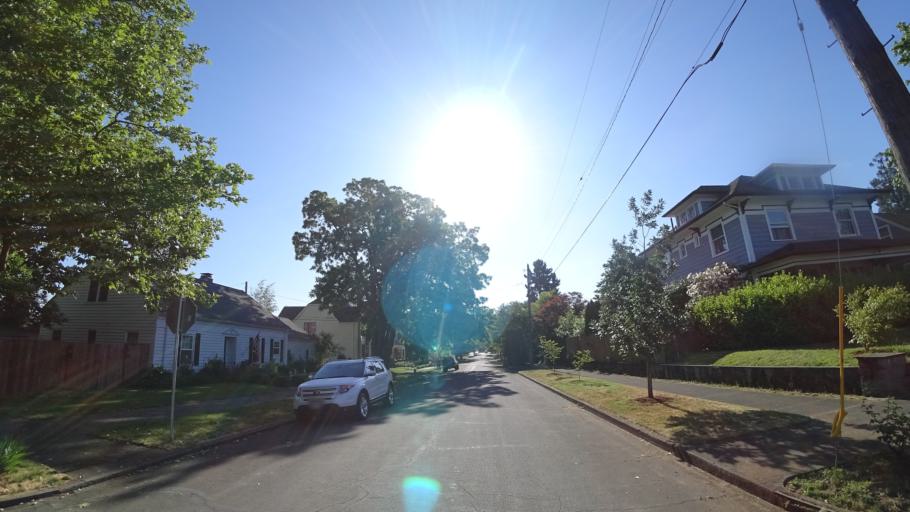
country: US
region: Oregon
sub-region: Multnomah County
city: Portland
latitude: 45.5690
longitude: -122.6658
